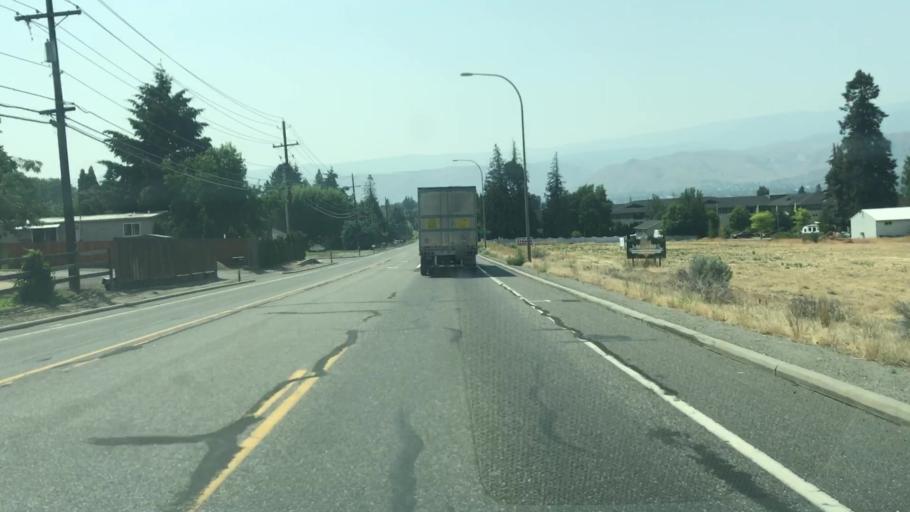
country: US
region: Washington
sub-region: Douglas County
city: East Wenatchee Bench
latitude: 47.4552
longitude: -120.2974
